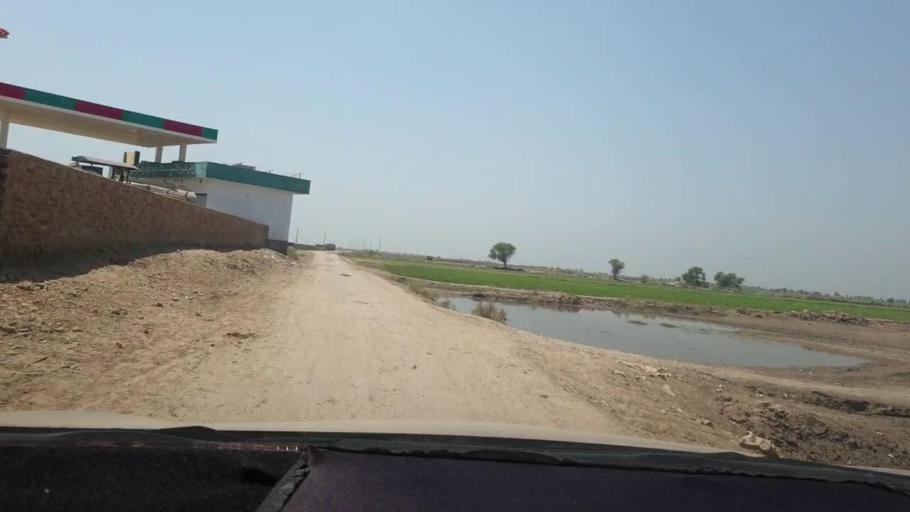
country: PK
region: Sindh
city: Shahdadkot
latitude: 27.8340
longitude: 67.8899
